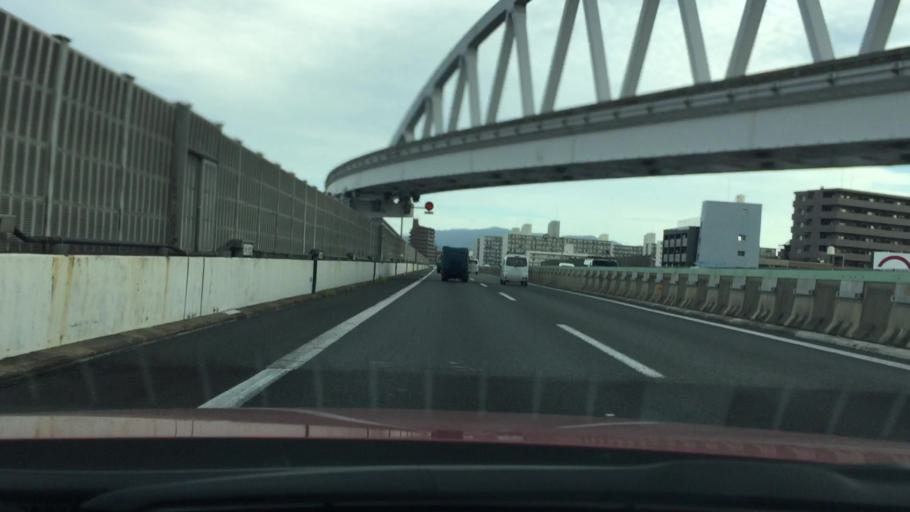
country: JP
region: Osaka
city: Ibaraki
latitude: 34.7944
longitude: 135.5657
